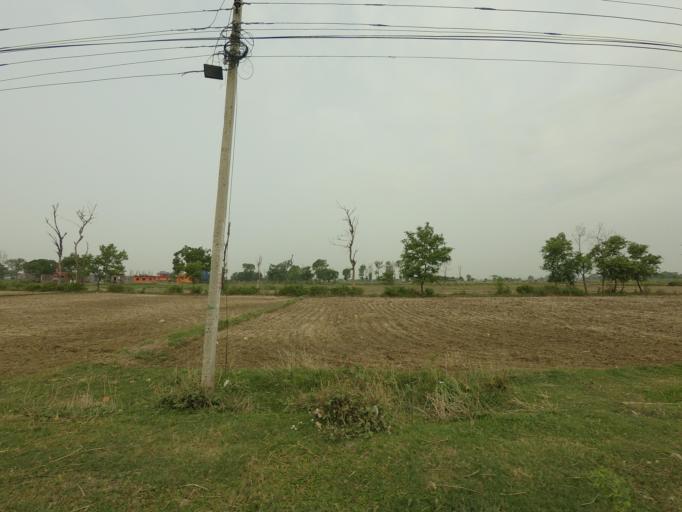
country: NP
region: Western Region
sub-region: Lumbini Zone
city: Bhairahawa
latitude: 27.4875
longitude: 83.4276
